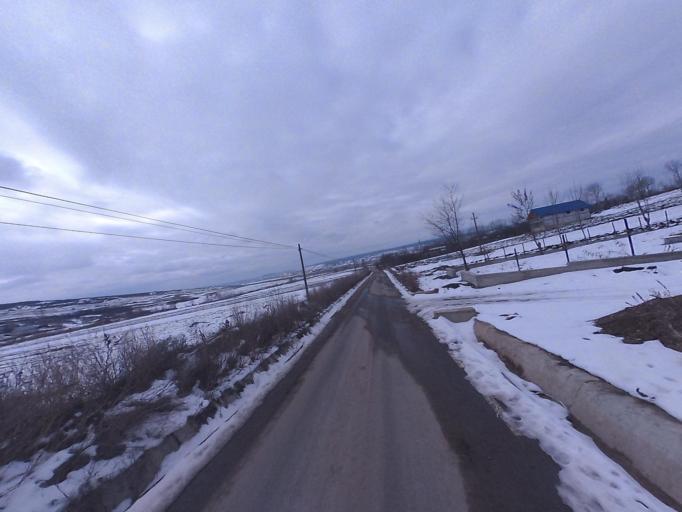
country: RO
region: Iasi
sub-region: Comuna Tibana
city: Tibana
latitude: 46.9837
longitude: 27.3522
